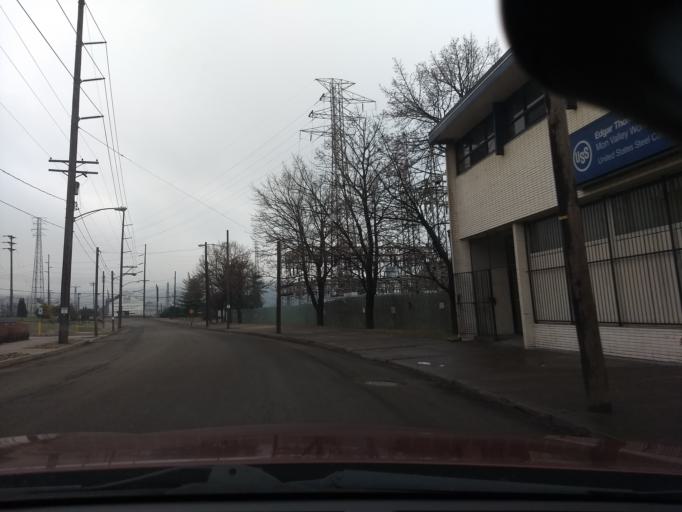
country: US
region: Pennsylvania
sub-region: Allegheny County
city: Braddock
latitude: 40.3977
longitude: -79.8609
